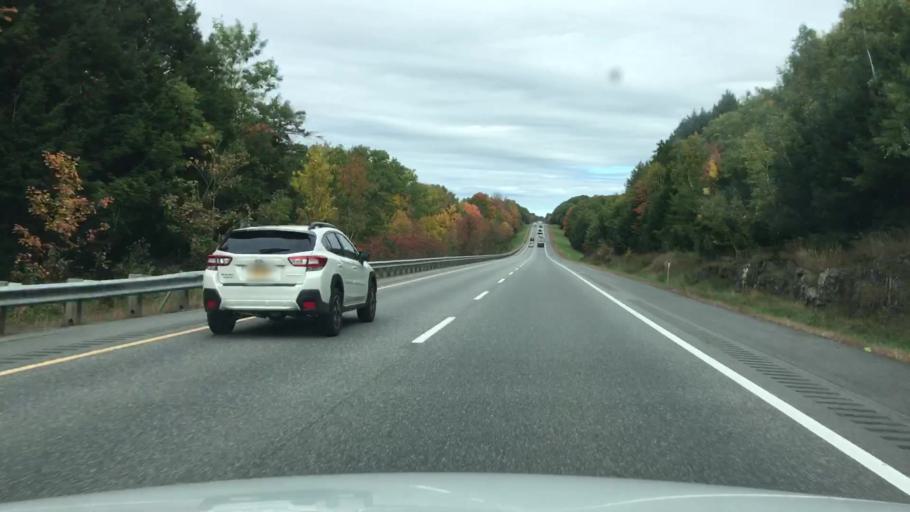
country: US
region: Maine
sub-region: Kennebec County
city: Sidney
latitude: 44.3981
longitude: -69.7538
